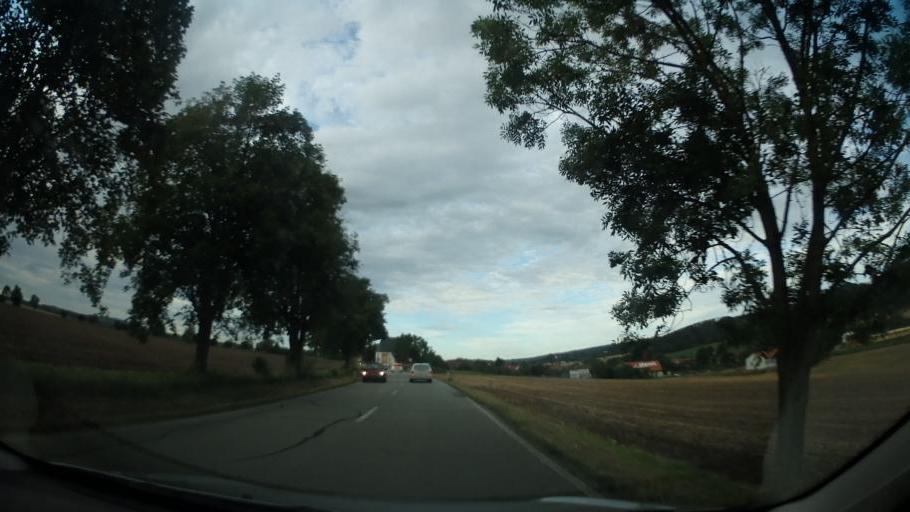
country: CZ
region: South Moravian
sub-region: Okres Blansko
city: Boskovice
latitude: 49.5280
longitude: 16.6850
